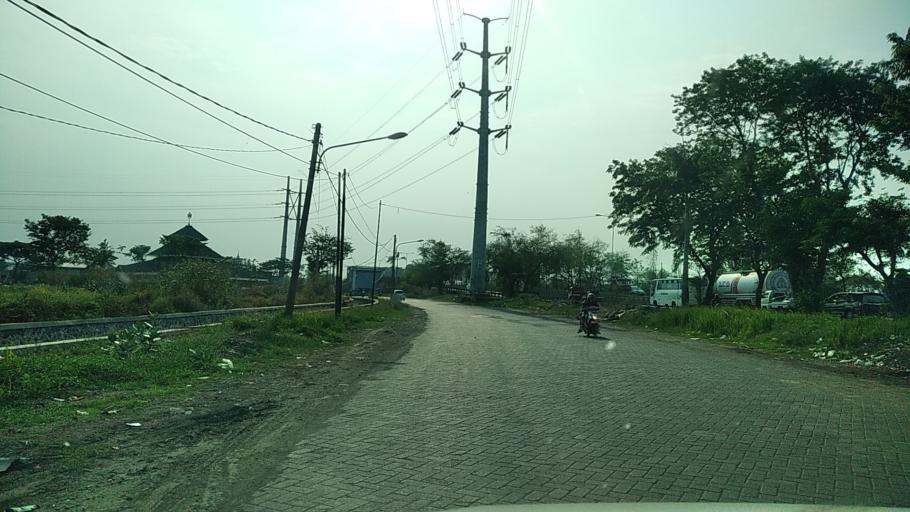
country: ID
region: Central Java
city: Semarang
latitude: -6.9544
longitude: 110.4009
